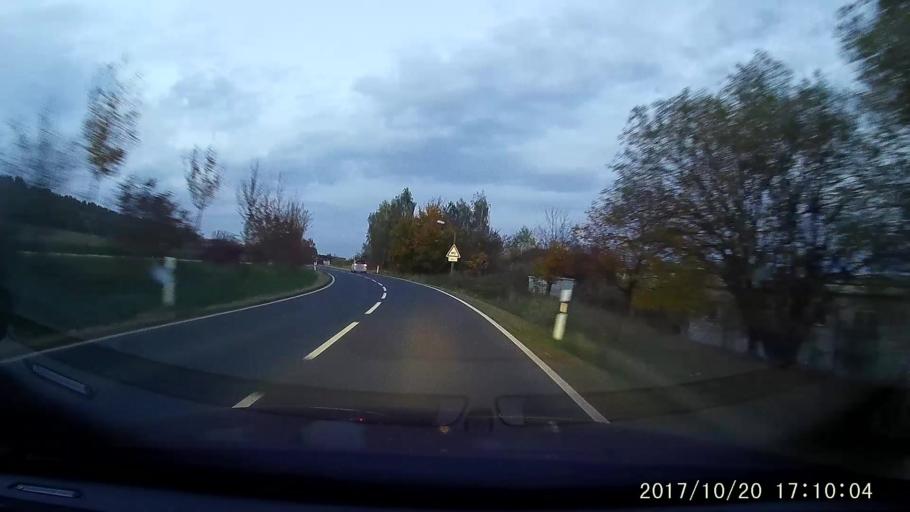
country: DE
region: Saxony
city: Goerlitz
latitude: 51.1227
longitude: 14.9409
